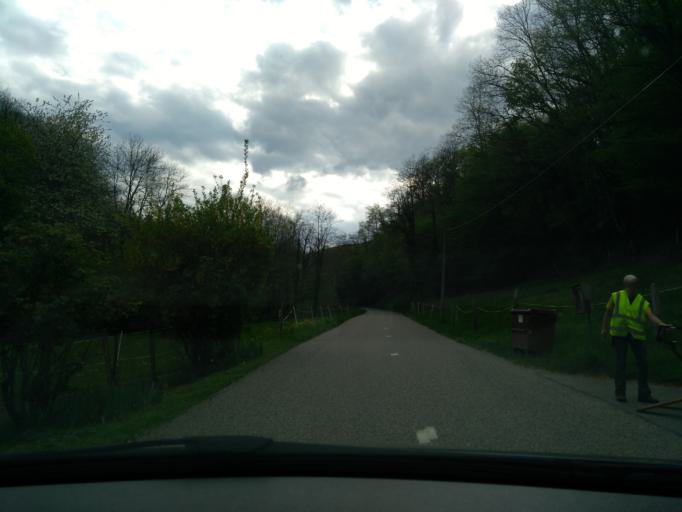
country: FR
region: Rhone-Alpes
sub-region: Departement de la Haute-Savoie
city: Moye
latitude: 45.8414
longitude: 5.9101
